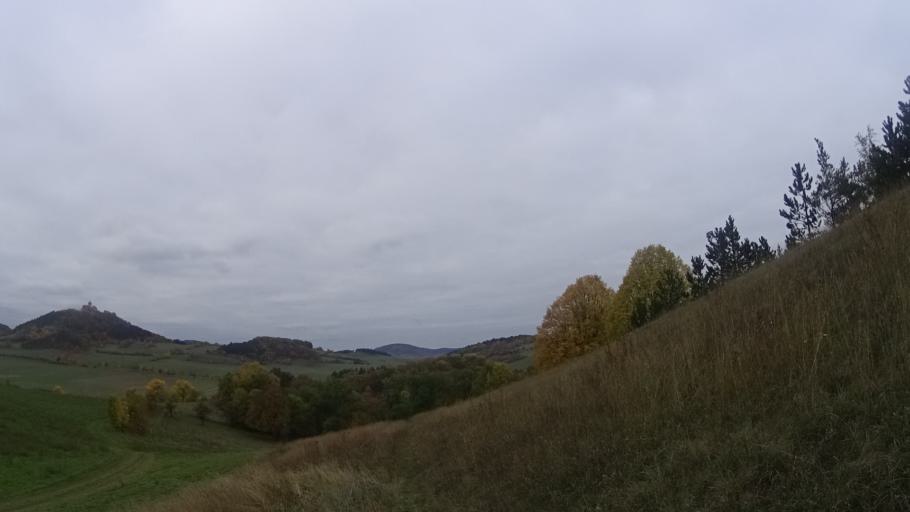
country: DE
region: Thuringia
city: Apfelstadt
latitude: 50.8591
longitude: 10.8981
